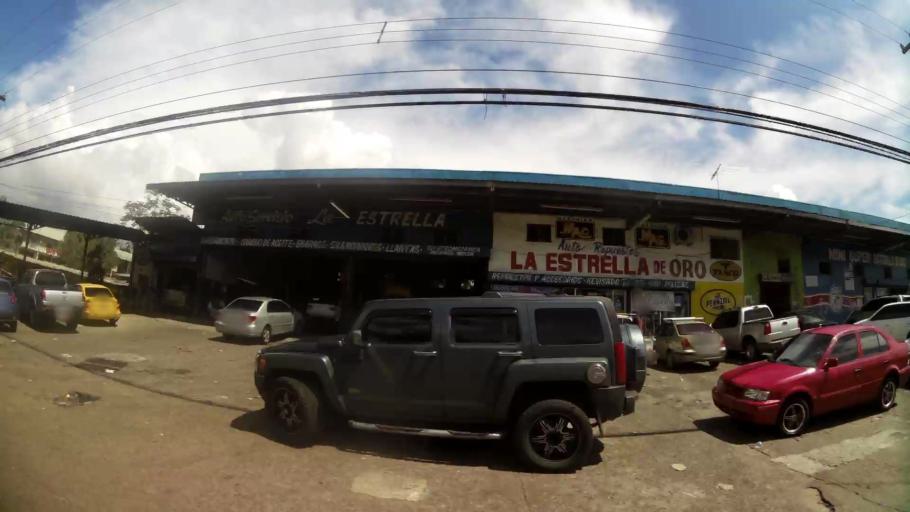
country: PA
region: Panama
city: Vista Alegre
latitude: 8.9280
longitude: -79.7008
